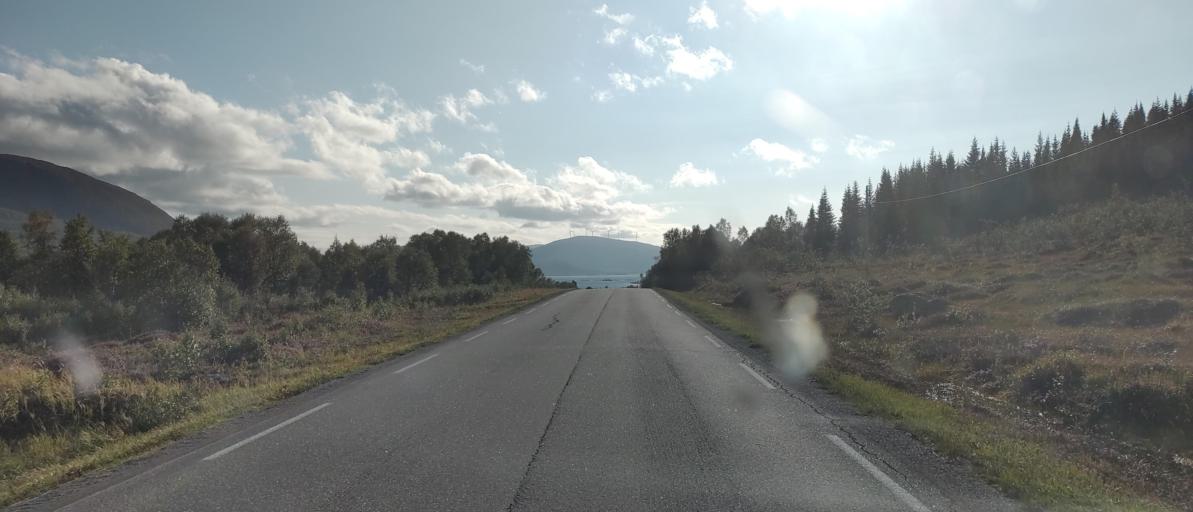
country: NO
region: Nordland
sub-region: Sortland
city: Sortland
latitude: 68.7916
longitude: 15.5051
